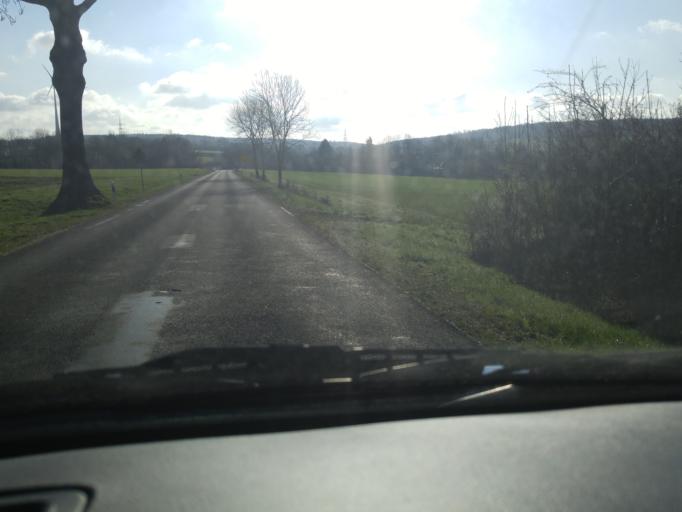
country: DE
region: Hesse
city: Herbstein
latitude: 50.5822
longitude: 9.3569
